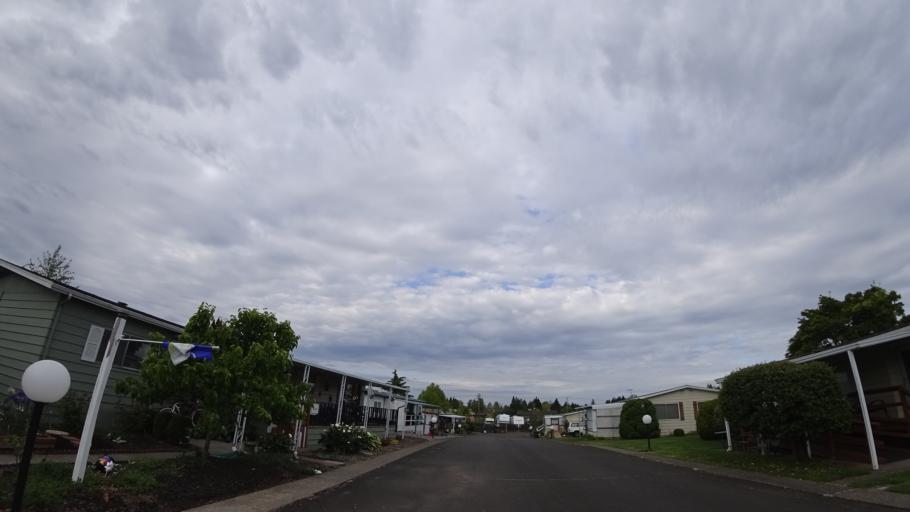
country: US
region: Oregon
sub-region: Washington County
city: Hillsboro
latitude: 45.5027
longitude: -122.9564
